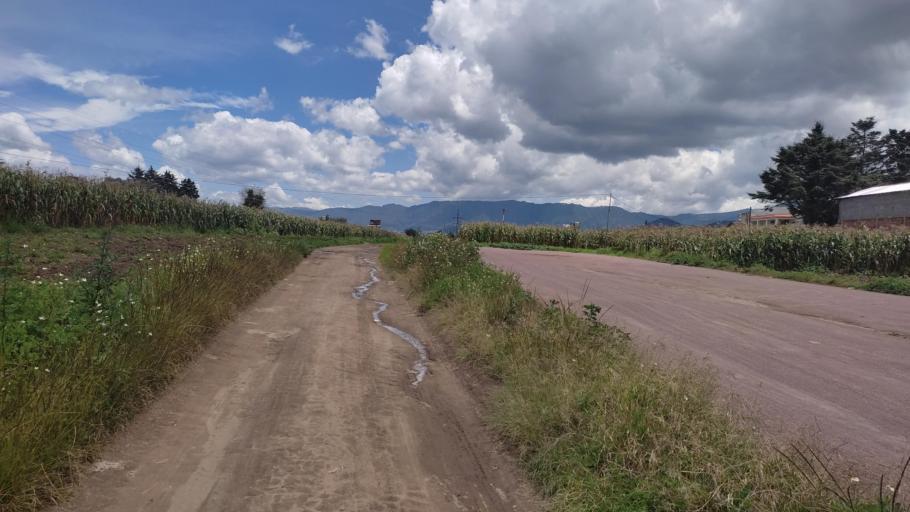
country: GT
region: Quetzaltenango
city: Quetzaltenango
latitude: 14.8586
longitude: -91.5289
